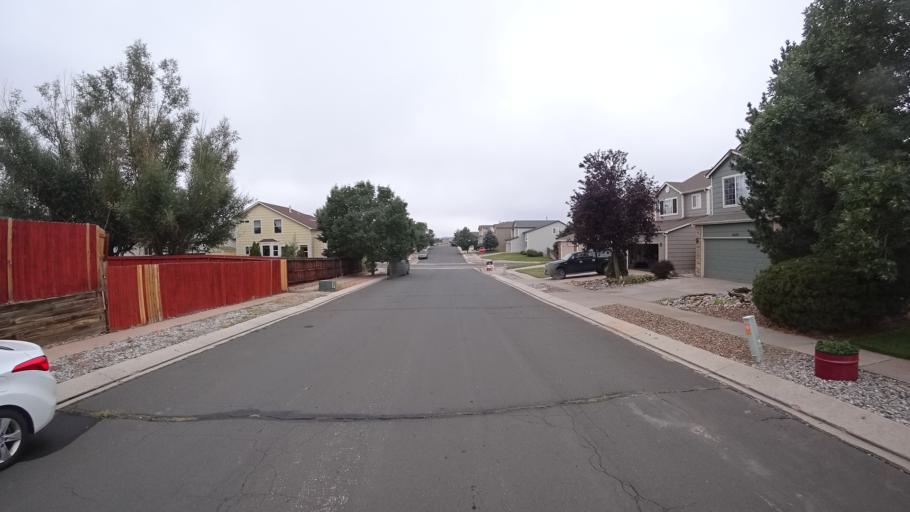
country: US
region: Colorado
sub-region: El Paso County
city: Black Forest
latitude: 38.9364
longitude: -104.7437
